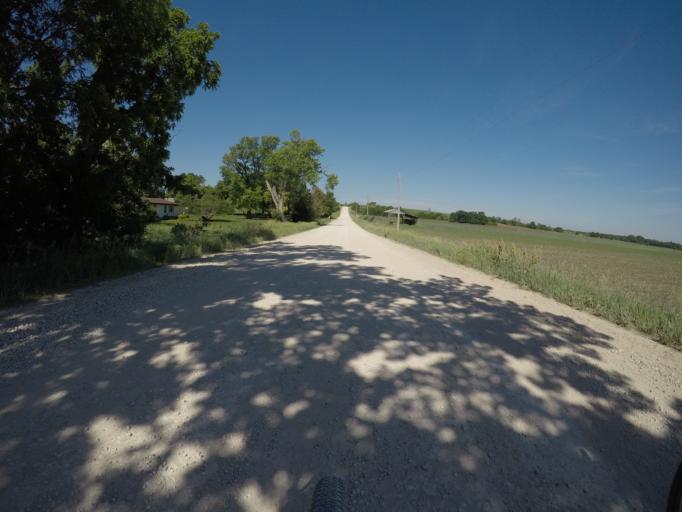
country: US
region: Kansas
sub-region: Wabaunsee County
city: Alma
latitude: 39.0152
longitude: -96.1336
